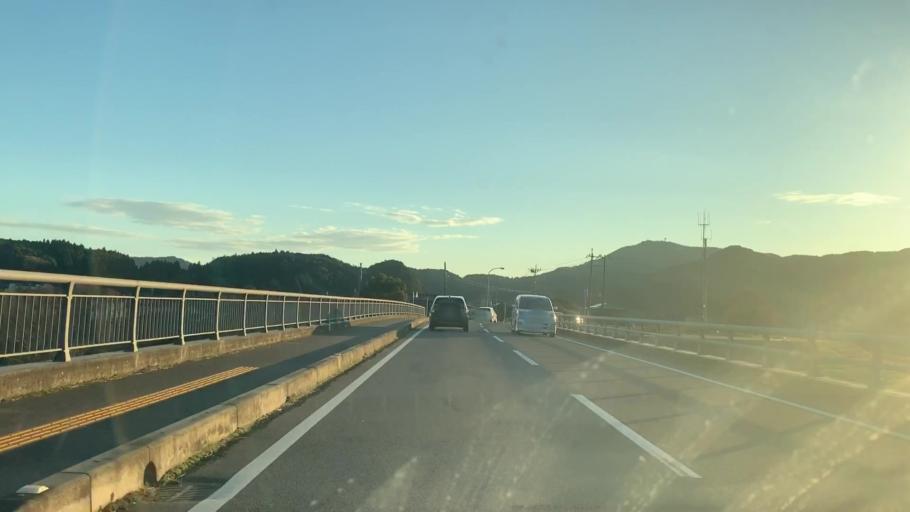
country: JP
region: Saga Prefecture
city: Imaricho-ko
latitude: 33.3089
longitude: 129.9706
